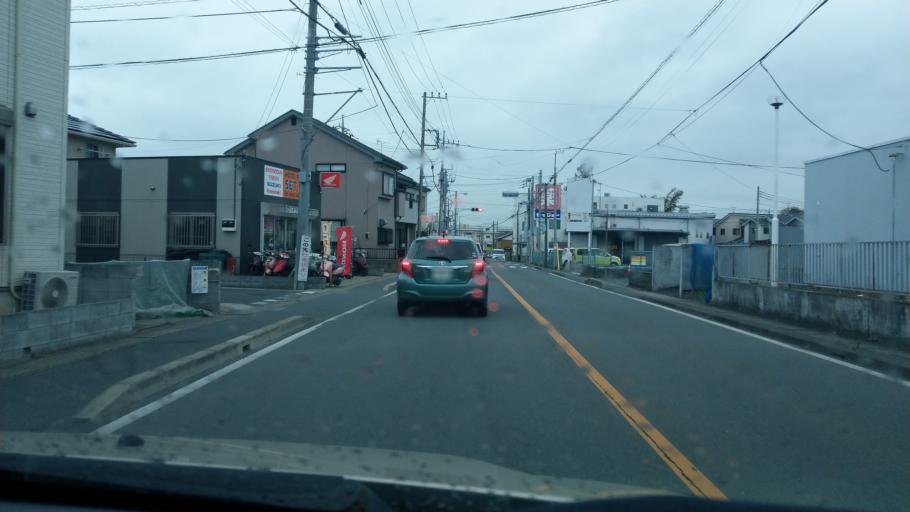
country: JP
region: Saitama
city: Iwatsuki
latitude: 35.9316
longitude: 139.6734
